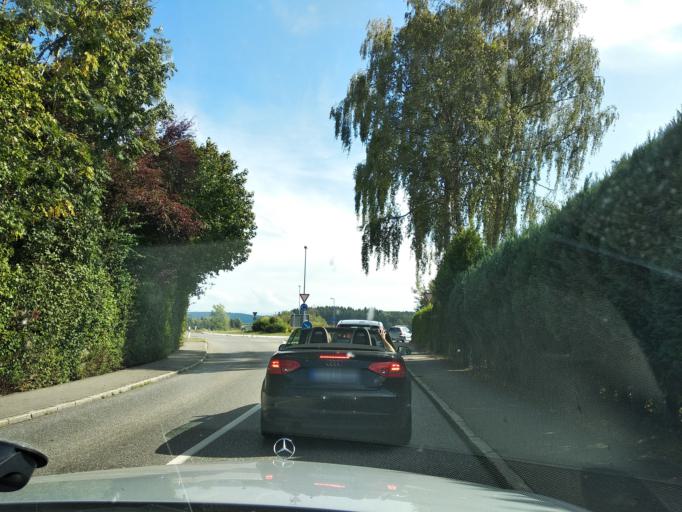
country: DE
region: Baden-Wuerttemberg
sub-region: Tuebingen Region
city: Amtzell
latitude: 47.6676
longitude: 9.7663
